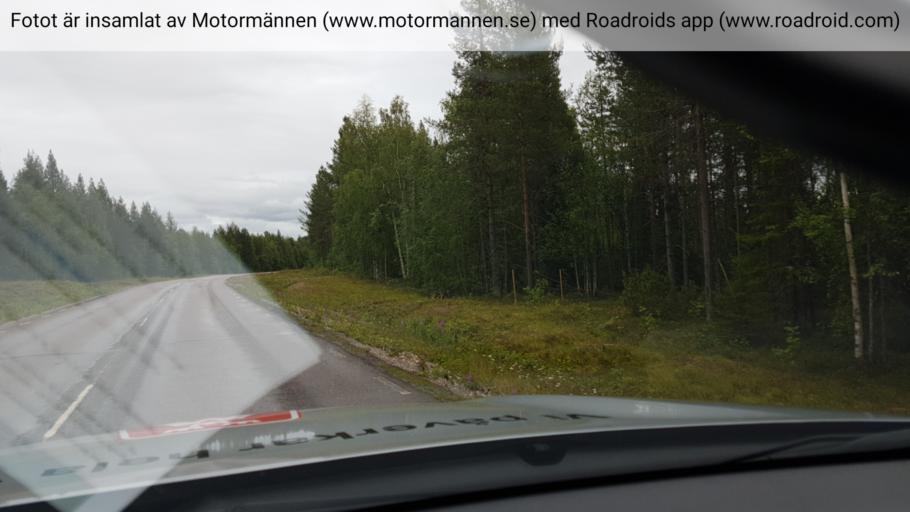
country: SE
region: Norrbotten
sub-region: Overkalix Kommun
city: OEverkalix
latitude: 67.0612
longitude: 22.2859
